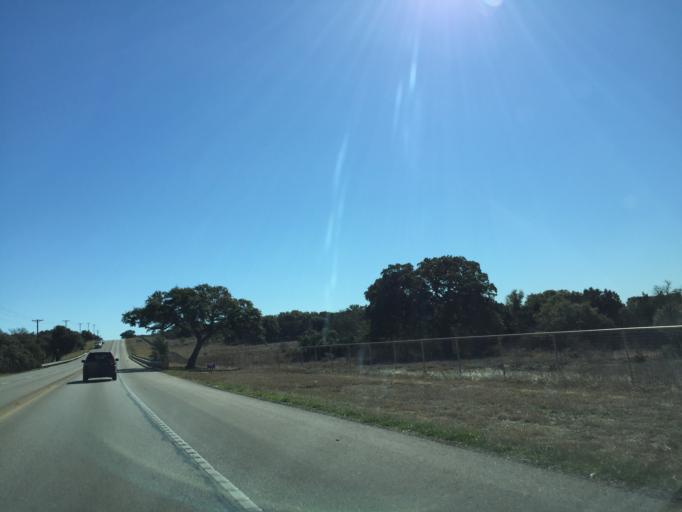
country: US
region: Texas
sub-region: Comal County
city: Canyon Lake
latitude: 29.7773
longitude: -98.3103
